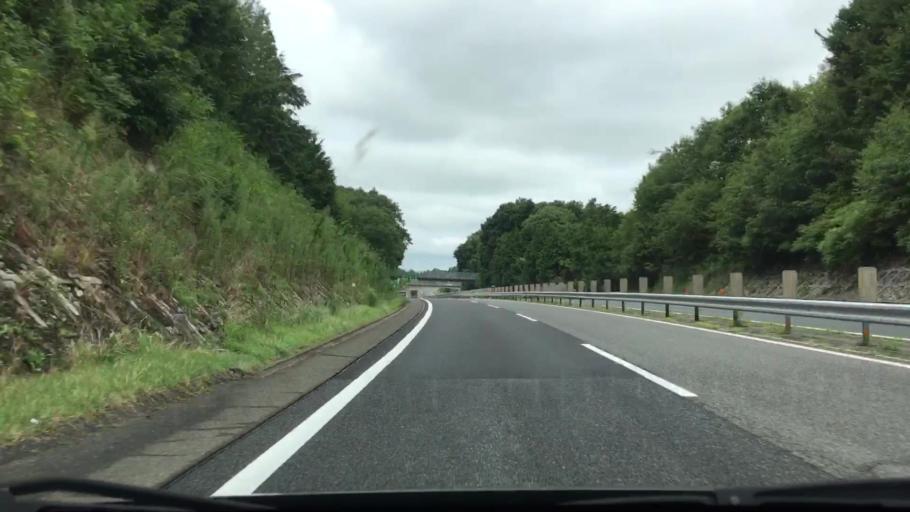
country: JP
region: Hiroshima
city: Shobara
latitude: 34.8312
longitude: 132.9646
